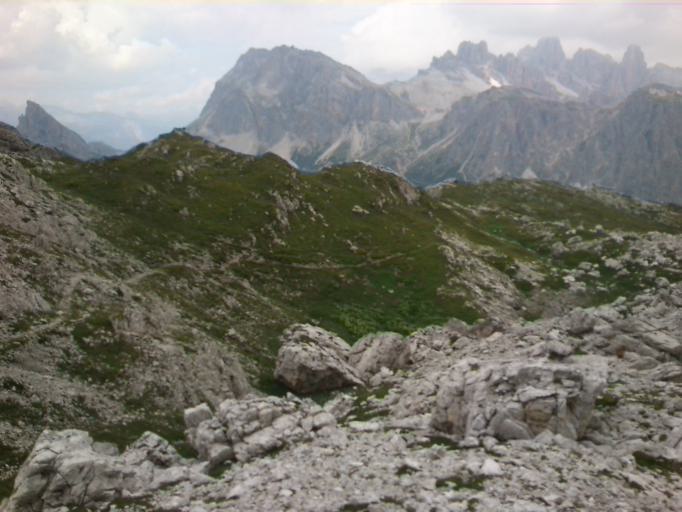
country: IT
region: Veneto
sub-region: Provincia di Belluno
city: Selva di Cadore
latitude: 46.5029
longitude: 12.0336
